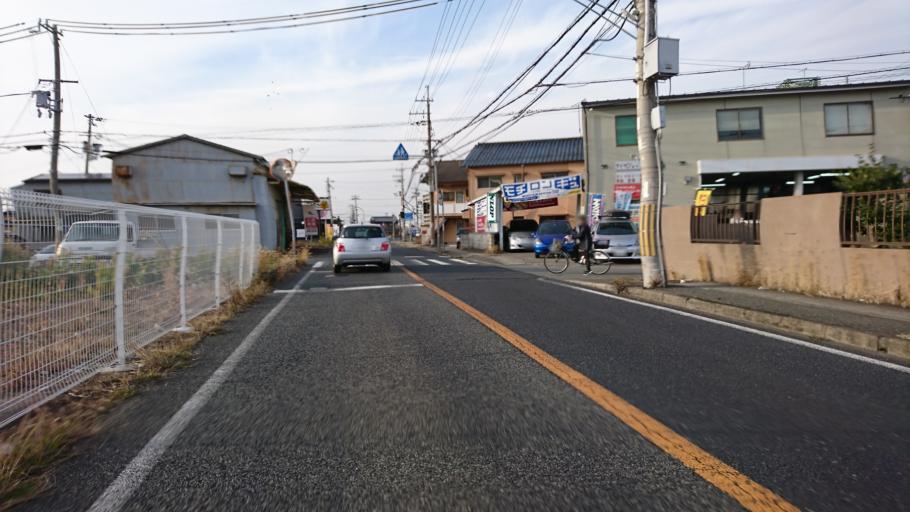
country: JP
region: Hyogo
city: Kakogawacho-honmachi
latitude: 34.7114
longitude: 134.8641
